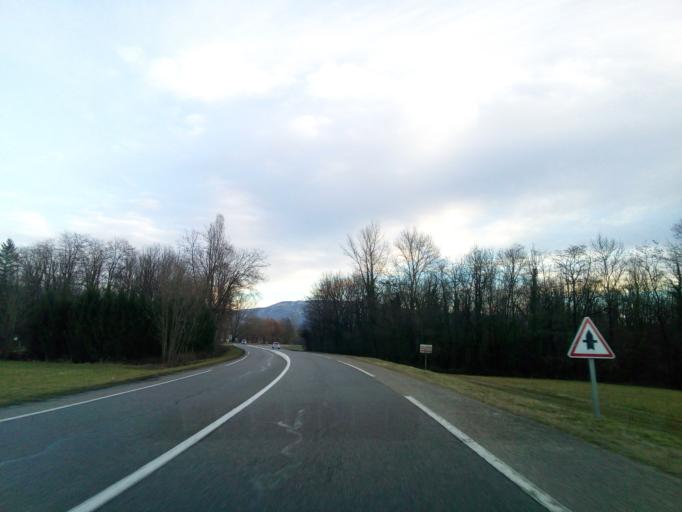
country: FR
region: Rhone-Alpes
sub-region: Departement de l'Isere
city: Romagnieu
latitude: 45.5711
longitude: 5.6556
